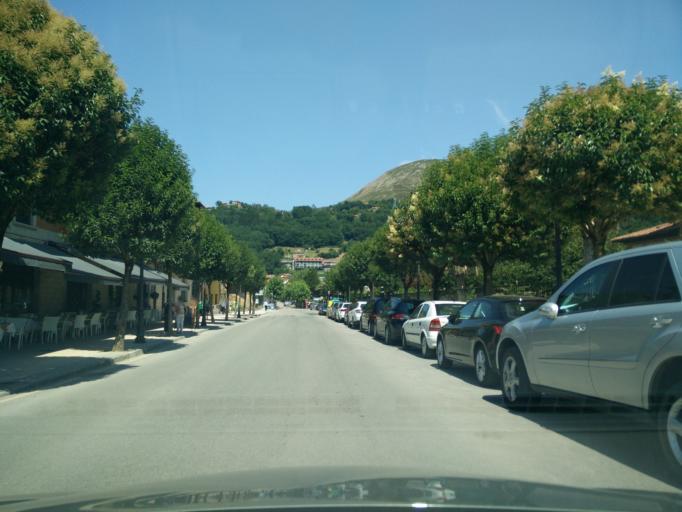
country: ES
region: Asturias
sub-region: Province of Asturias
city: Cangas de Onis
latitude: 43.3519
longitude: -5.1302
